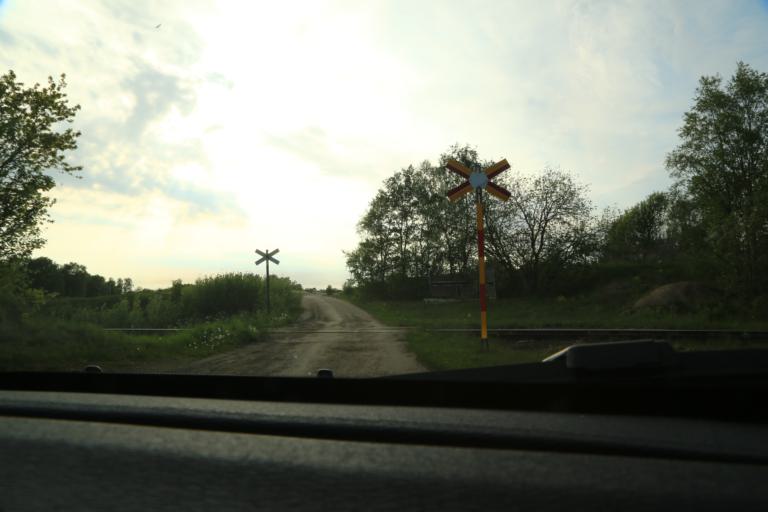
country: SE
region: Halland
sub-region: Kungsbacka Kommun
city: Frillesas
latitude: 57.2384
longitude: 12.1875
